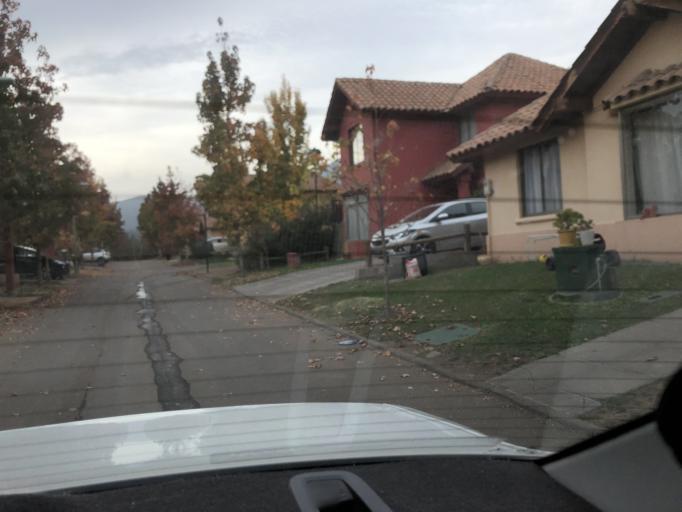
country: CL
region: Santiago Metropolitan
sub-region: Provincia de Cordillera
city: Puente Alto
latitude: -33.5891
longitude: -70.5116
